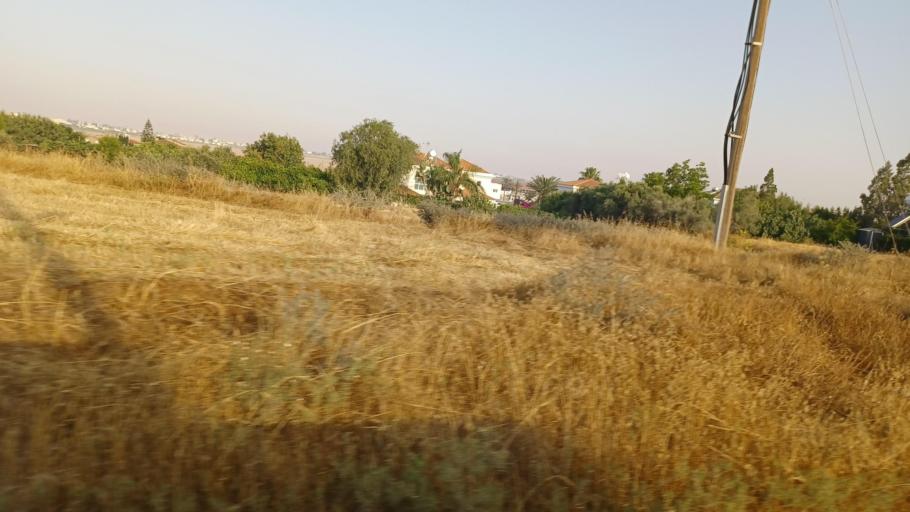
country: CY
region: Ammochostos
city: Paralimni
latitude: 35.0310
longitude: 33.9785
